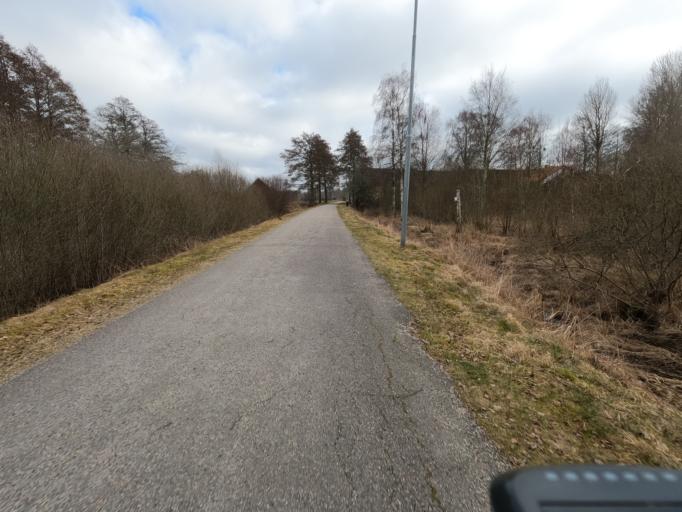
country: SE
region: Joenkoeping
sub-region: Varnamo Kommun
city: Rydaholm
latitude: 56.8620
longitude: 14.1709
